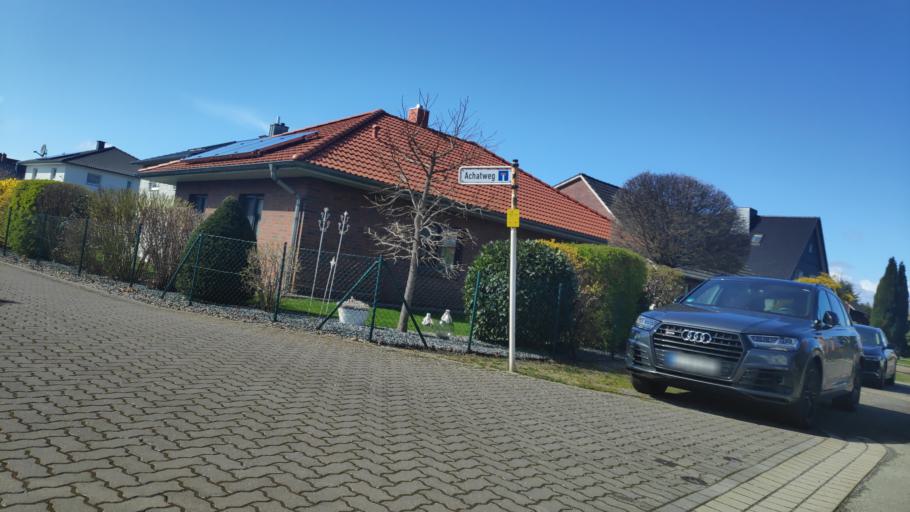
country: DE
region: North Rhine-Westphalia
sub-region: Regierungsbezirk Detmold
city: Minden
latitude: 52.3106
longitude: 8.9057
